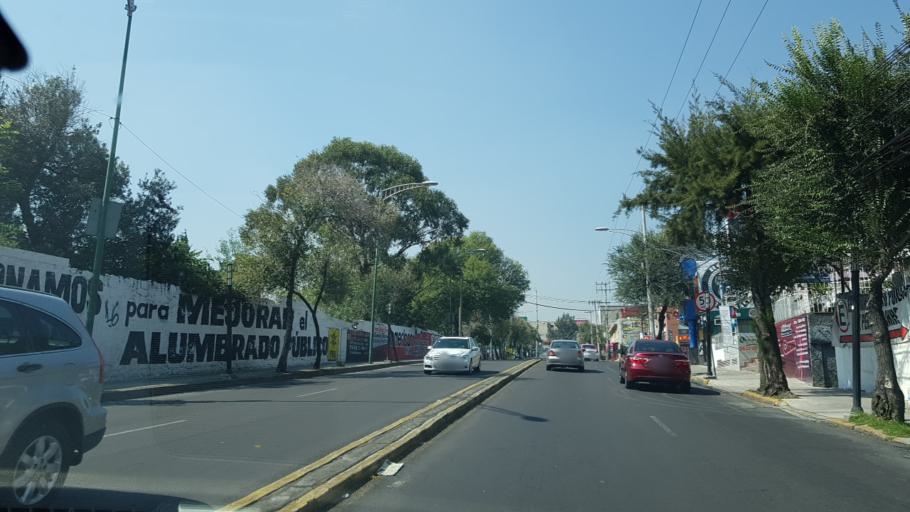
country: MX
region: Mexico City
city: Alvaro Obregon
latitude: 19.3523
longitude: -99.2165
